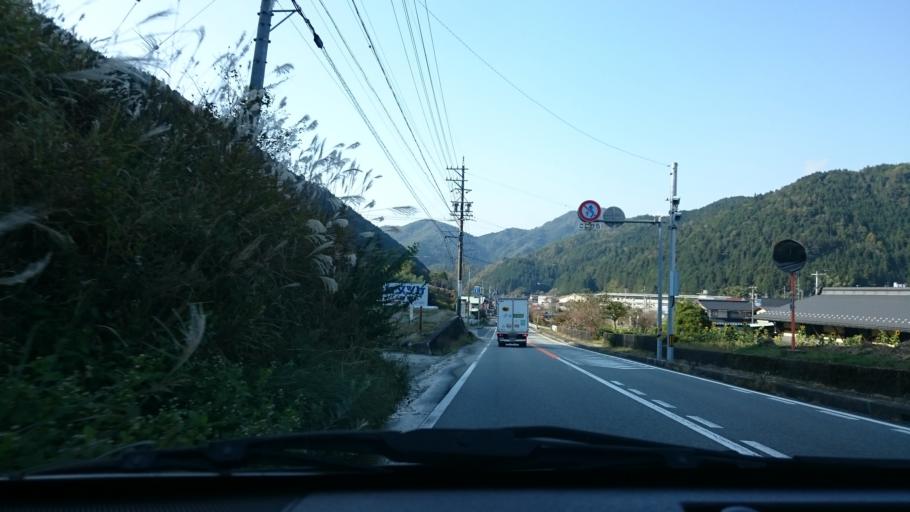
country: JP
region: Gifu
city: Gujo
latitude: 35.7644
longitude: 137.2896
